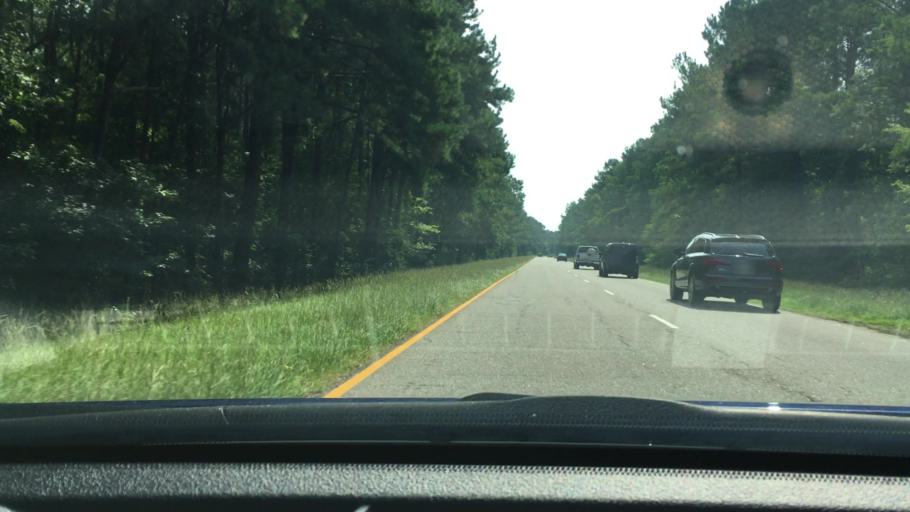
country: US
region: South Carolina
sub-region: Sumter County
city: Stateburg
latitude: 33.9521
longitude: -80.5731
